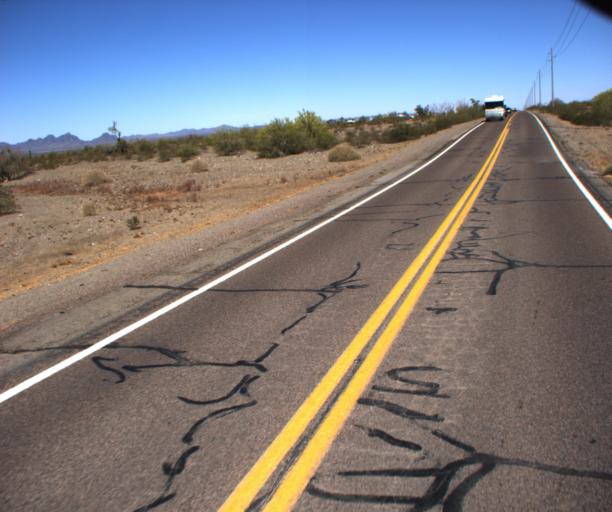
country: US
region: Arizona
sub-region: La Paz County
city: Salome
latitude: 33.7738
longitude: -113.7971
